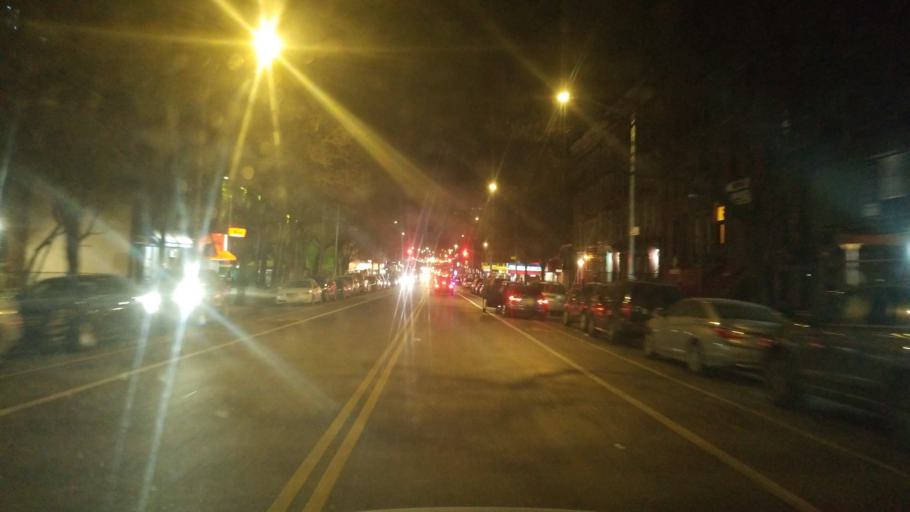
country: US
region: New York
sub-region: New York County
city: Manhattan
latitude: 40.8084
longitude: -73.9212
